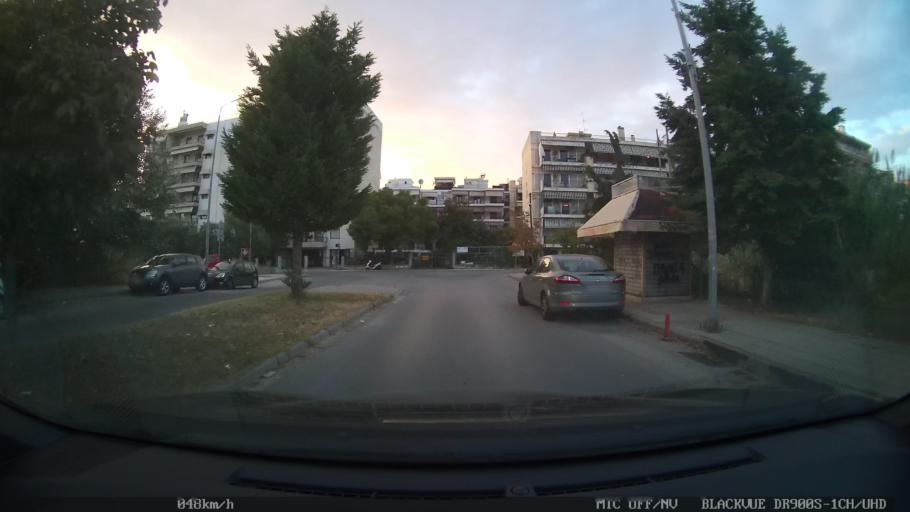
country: GR
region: Central Macedonia
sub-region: Nomos Thessalonikis
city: Pylaia
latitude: 40.6063
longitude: 22.9855
